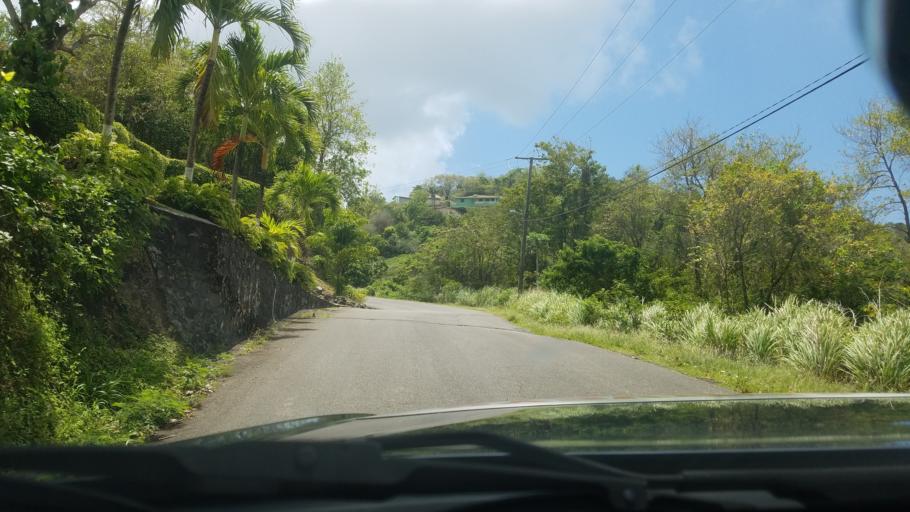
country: LC
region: Gros-Islet
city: Gros Islet
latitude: 14.0558
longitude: -60.9332
